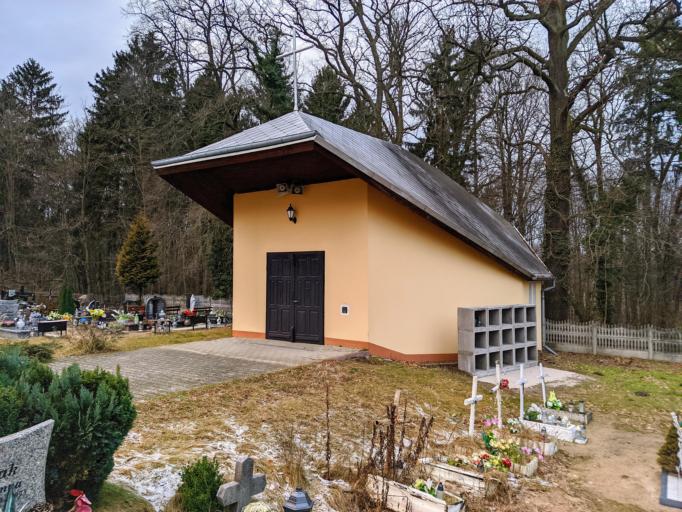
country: PL
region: Lubusz
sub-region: Zielona Gora
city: Zielona Gora
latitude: 51.9284
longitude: 15.6098
